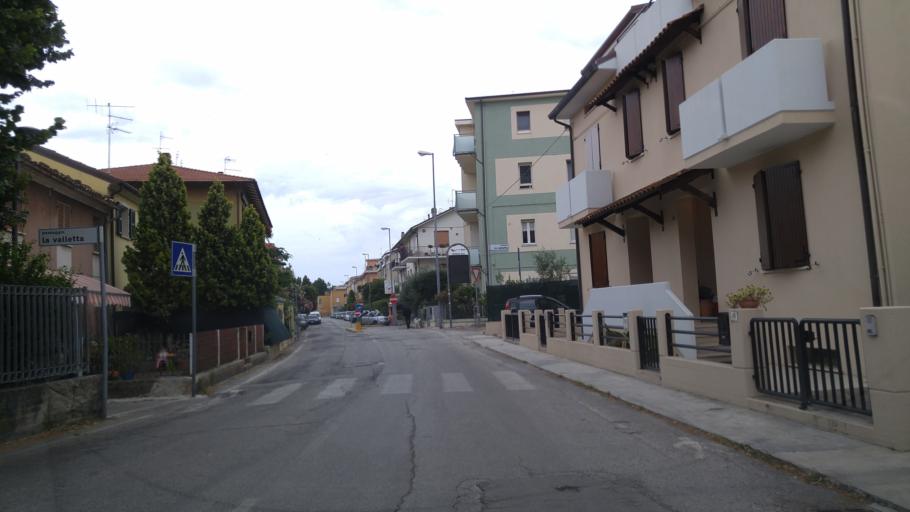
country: IT
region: The Marches
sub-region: Provincia di Pesaro e Urbino
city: Pesaro
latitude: 43.9192
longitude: 12.8992
